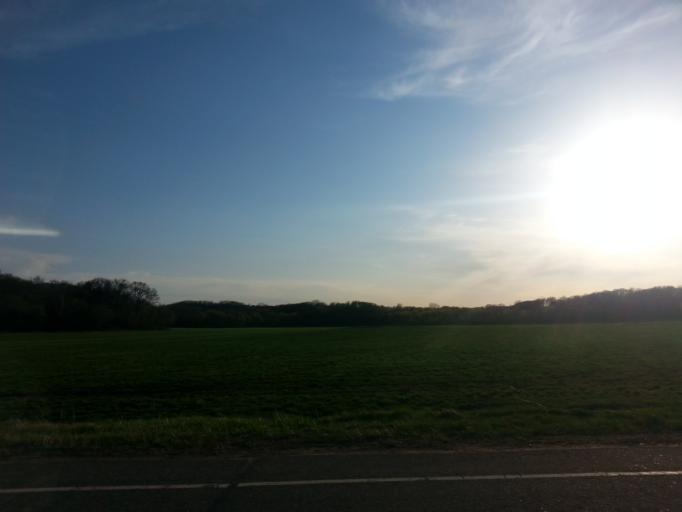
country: US
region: Wisconsin
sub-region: Pierce County
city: River Falls
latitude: 44.8978
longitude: -92.6724
